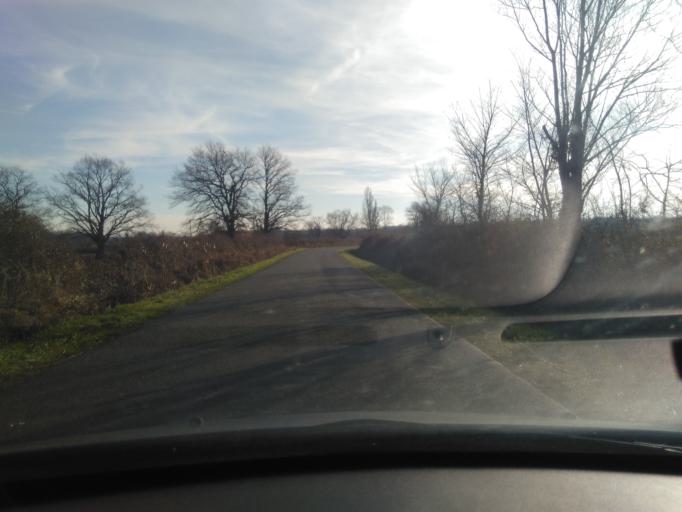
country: FR
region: Centre
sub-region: Departement du Cher
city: Orval
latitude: 46.6543
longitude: 2.4406
